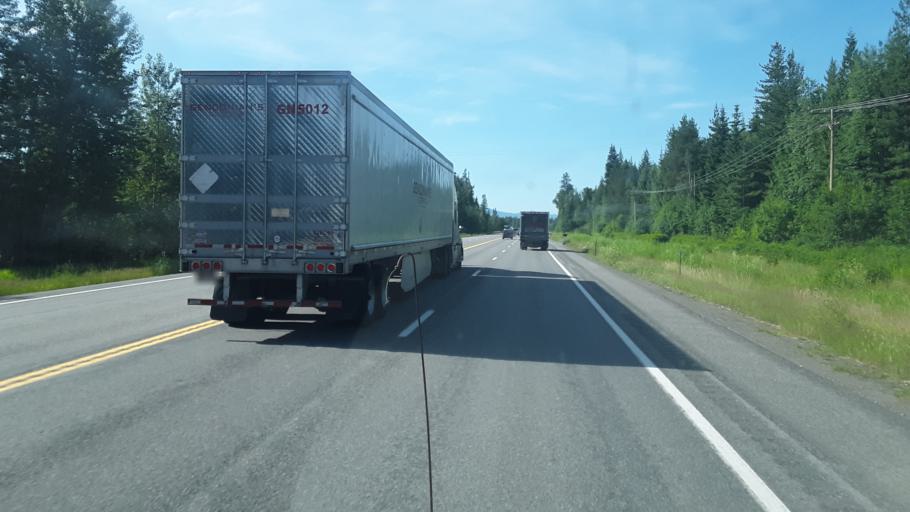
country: US
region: Idaho
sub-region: Bonner County
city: Ponderay
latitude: 48.3632
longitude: -116.5474
